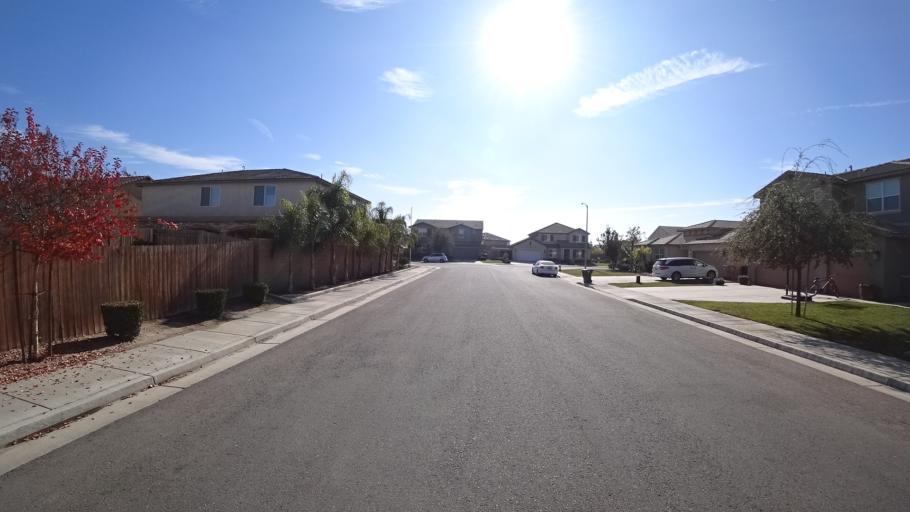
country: US
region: California
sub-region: Kern County
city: Greenfield
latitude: 35.2864
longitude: -119.0607
